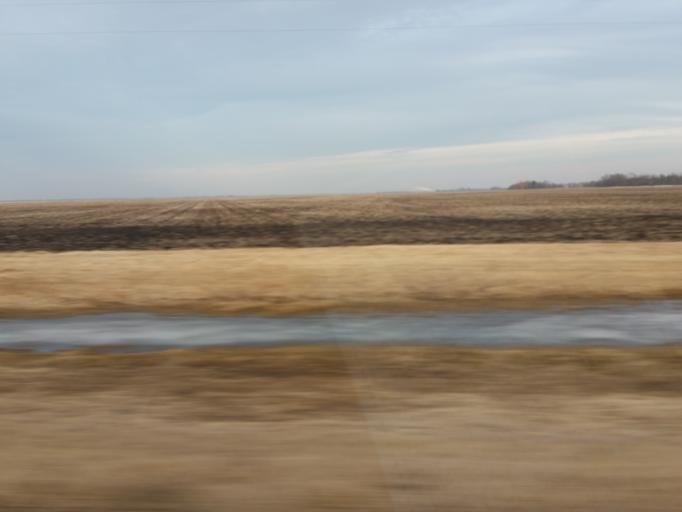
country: US
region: North Dakota
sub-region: Traill County
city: Mayville
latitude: 47.4444
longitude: -97.3260
